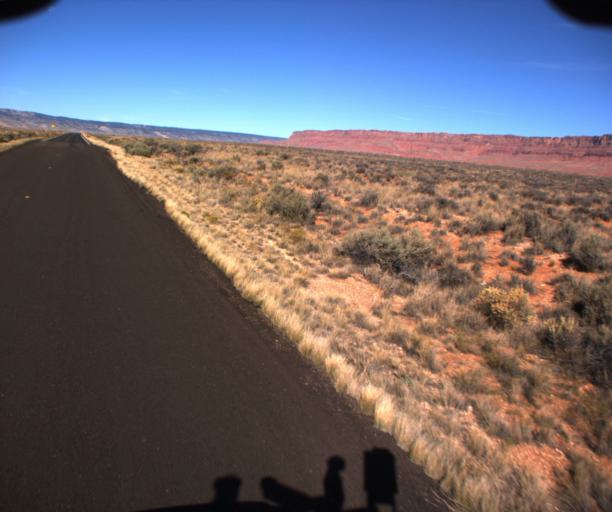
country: US
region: Arizona
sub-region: Coconino County
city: Page
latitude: 36.6923
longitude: -111.8927
